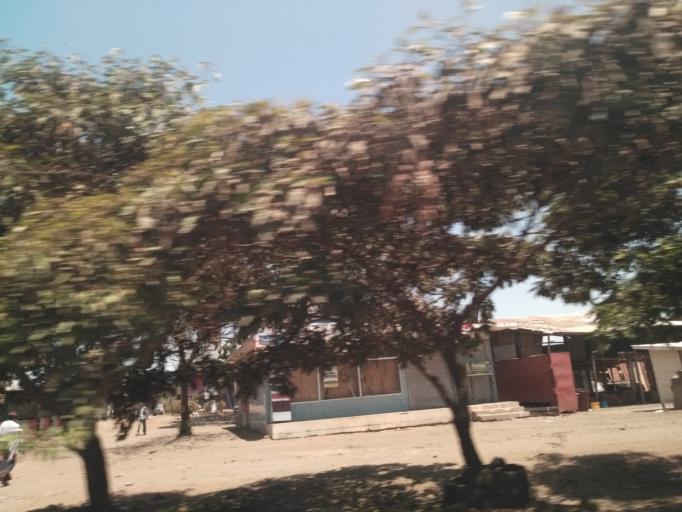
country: TZ
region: Arusha
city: Arusha
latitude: -3.3720
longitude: 36.6748
